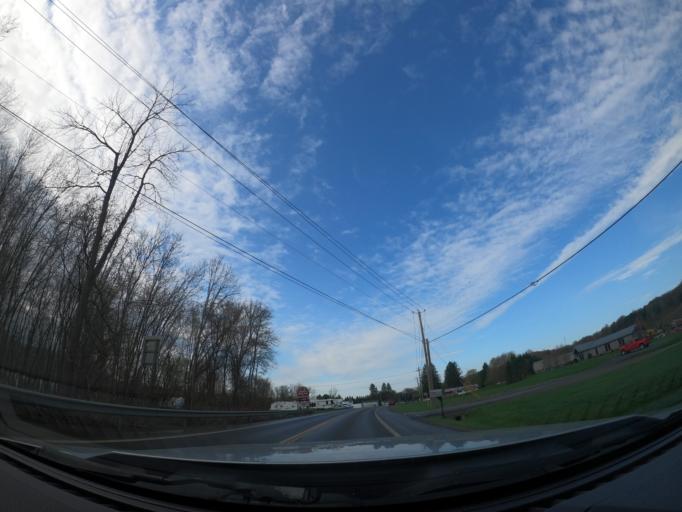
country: US
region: New York
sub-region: Cortland County
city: Homer
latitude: 42.6248
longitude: -76.1552
